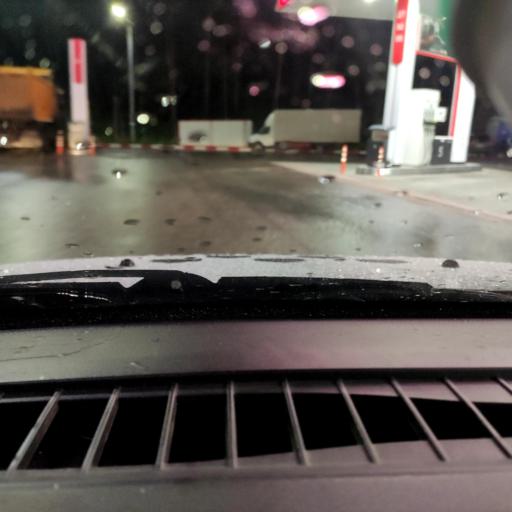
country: RU
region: Udmurtiya
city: Khokhryaki
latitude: 57.2001
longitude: 53.1567
